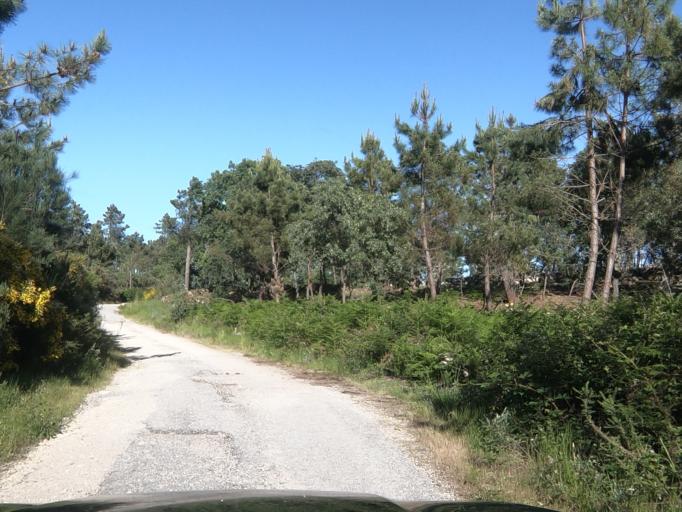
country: PT
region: Vila Real
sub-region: Sabrosa
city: Sabrosa
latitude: 41.3201
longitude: -7.6472
